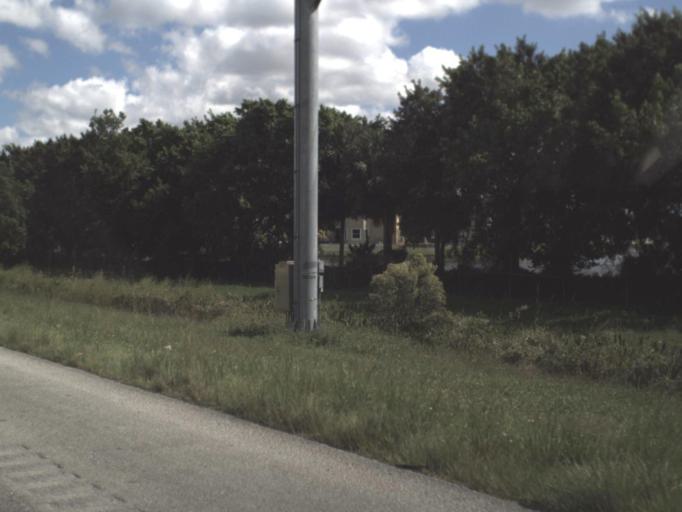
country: US
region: Florida
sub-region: Miami-Dade County
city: Country Club
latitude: 25.9601
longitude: -80.3373
